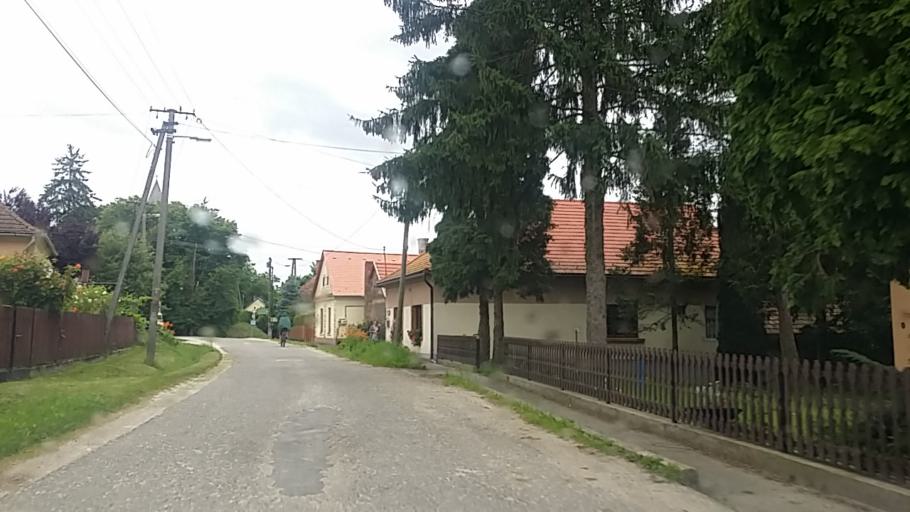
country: HU
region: Zala
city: Zalalovo
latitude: 46.8681
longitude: 16.5440
